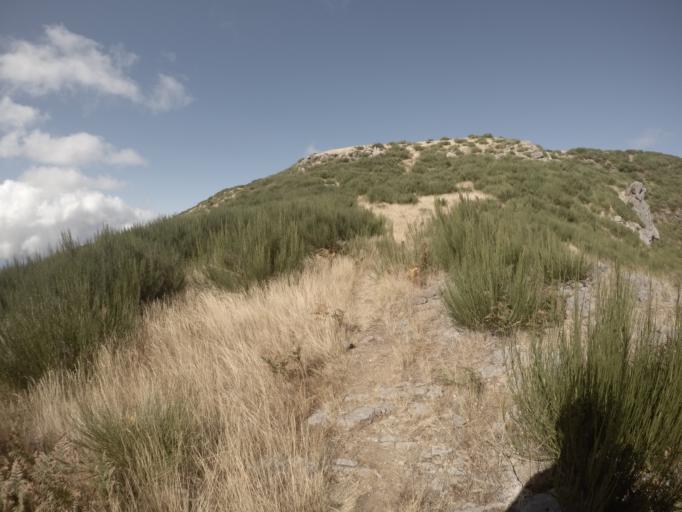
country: PT
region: Madeira
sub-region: Camara de Lobos
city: Curral das Freiras
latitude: 32.7141
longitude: -16.9897
